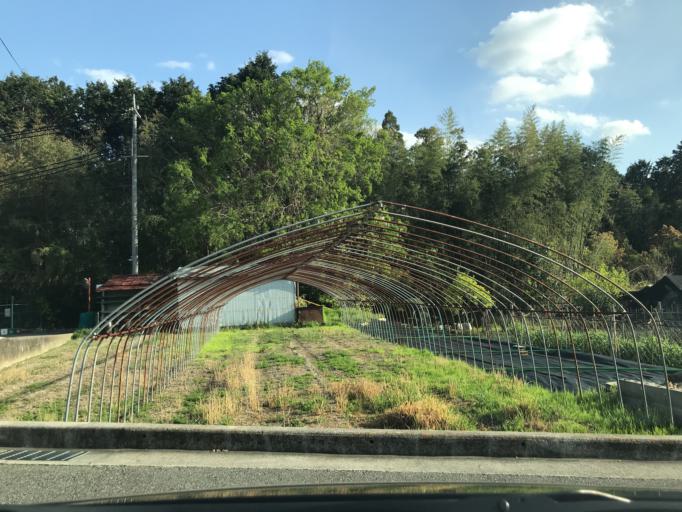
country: JP
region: Hyogo
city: Kawanishi
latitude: 34.8625
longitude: 135.4029
